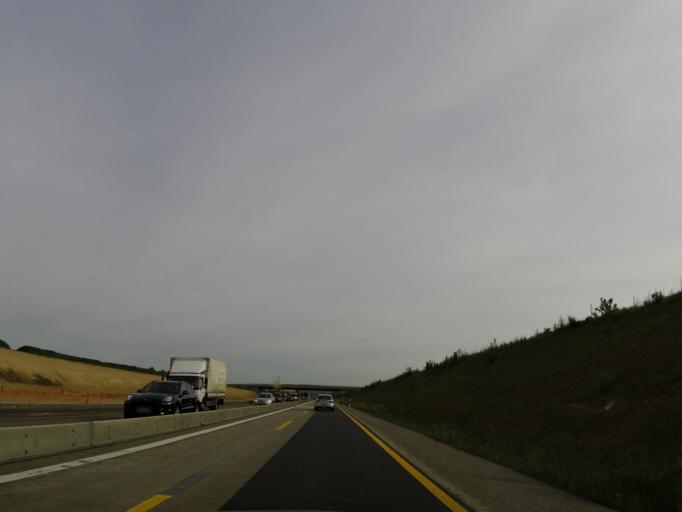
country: DE
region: Lower Saxony
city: Bockenem
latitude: 51.9866
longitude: 10.1544
